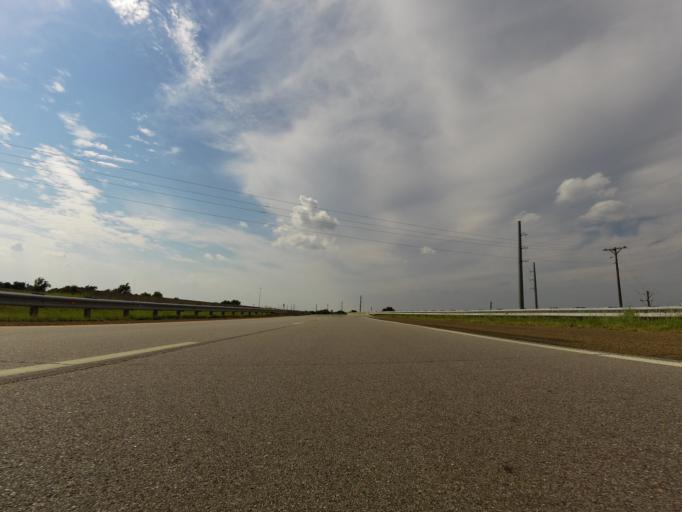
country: US
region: Kansas
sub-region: Sedgwick County
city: Maize
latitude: 37.7837
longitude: -97.4626
